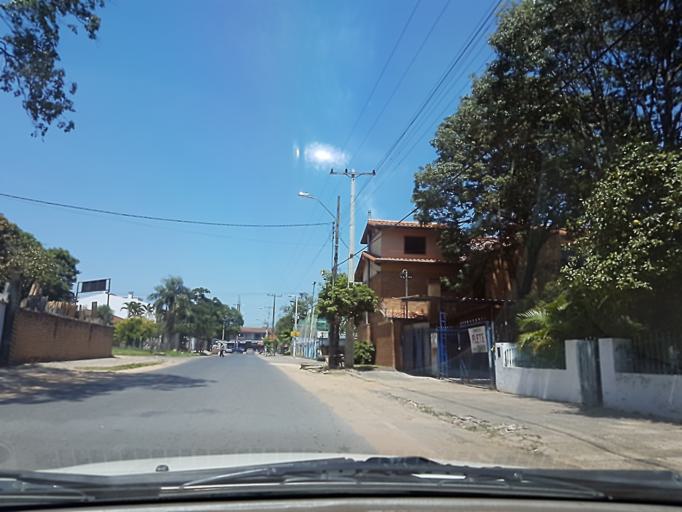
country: PY
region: Central
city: Fernando de la Mora
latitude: -25.2996
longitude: -57.5406
